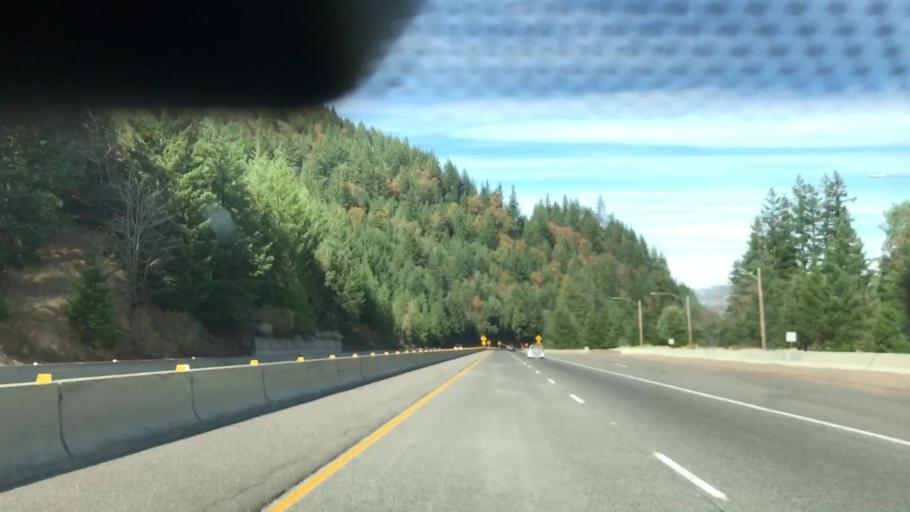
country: US
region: Oregon
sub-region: Jackson County
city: Ashland
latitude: 42.0851
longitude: -122.6007
